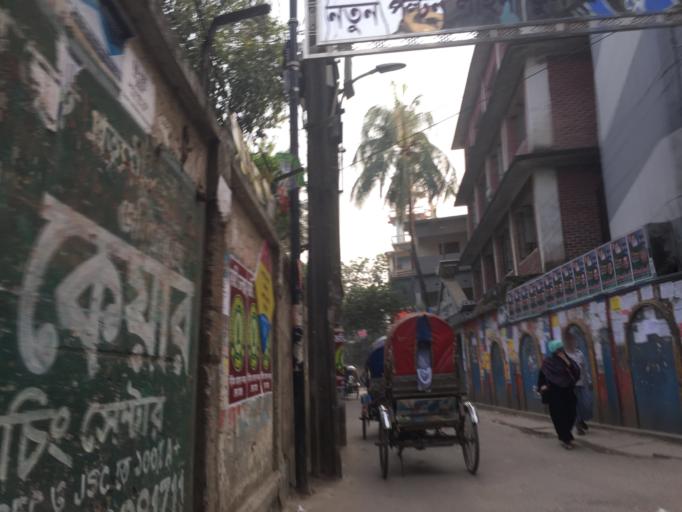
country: BD
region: Dhaka
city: Azimpur
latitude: 23.7278
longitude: 90.3813
